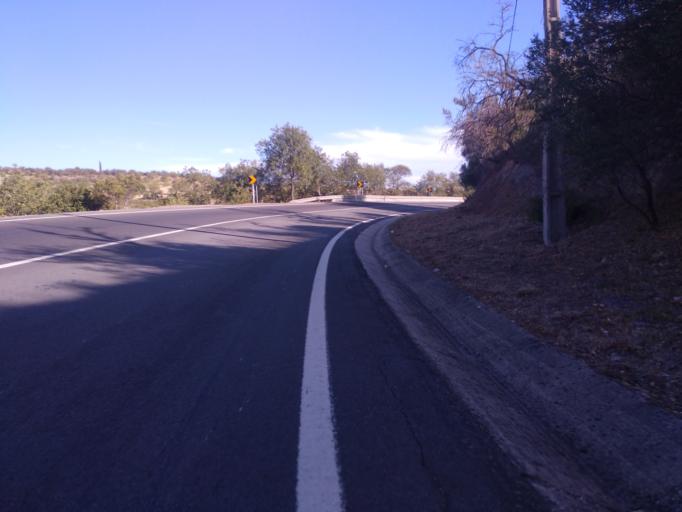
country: PT
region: Faro
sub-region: Sao Bras de Alportel
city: Sao Bras de Alportel
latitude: 37.1040
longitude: -7.9051
